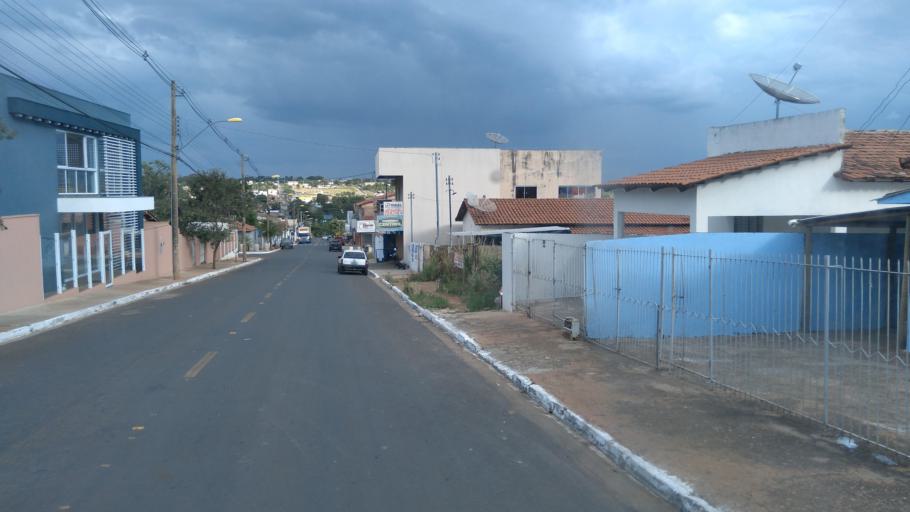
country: BR
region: Goias
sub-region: Mineiros
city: Mineiros
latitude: -17.5706
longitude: -52.5604
